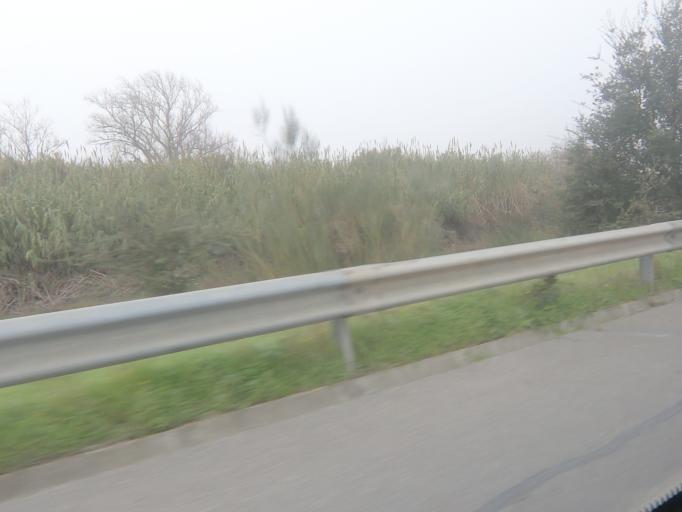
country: PT
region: Setubal
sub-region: Montijo
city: Montijo
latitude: 38.6839
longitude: -8.9487
